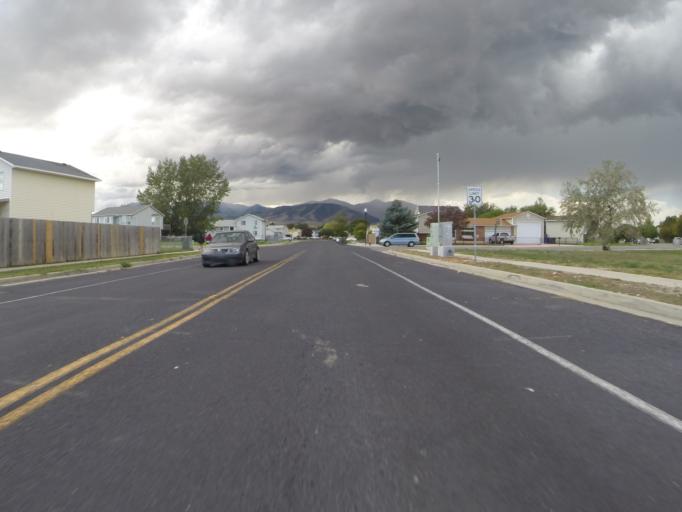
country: US
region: Utah
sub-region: Salt Lake County
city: West Valley City
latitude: 40.7044
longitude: -112.0372
